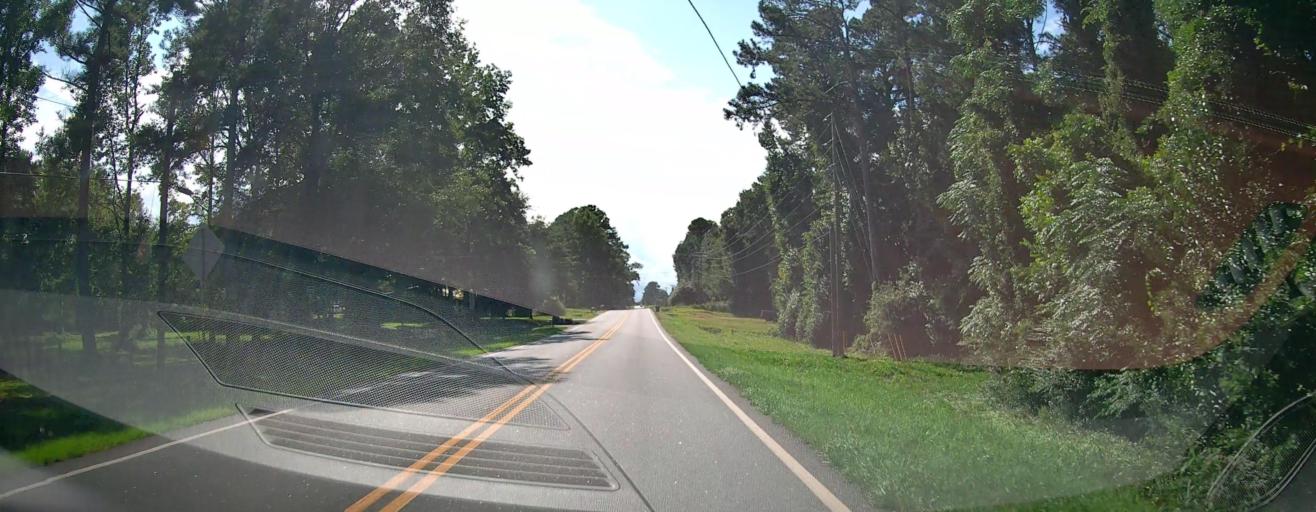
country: US
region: Georgia
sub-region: Upson County
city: Hannahs Mill
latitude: 32.8972
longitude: -84.3961
